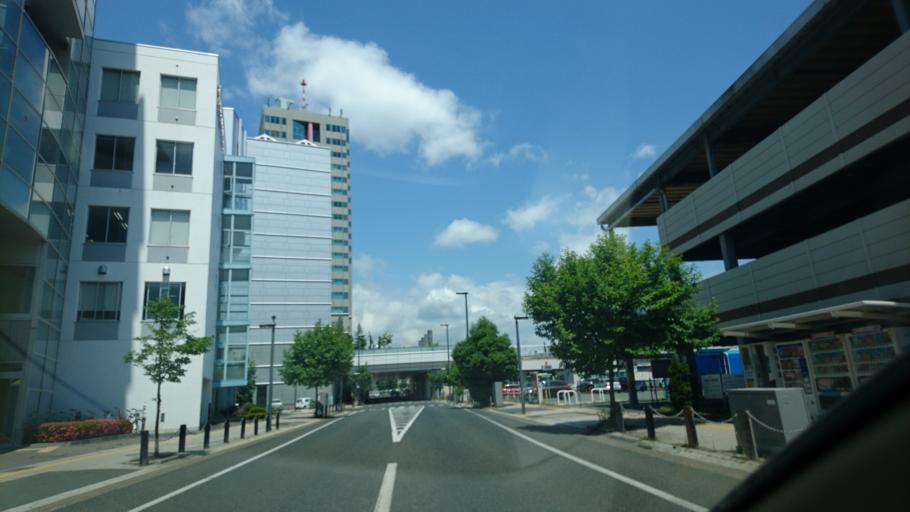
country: JP
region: Iwate
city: Morioka-shi
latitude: 39.7002
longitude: 141.1355
